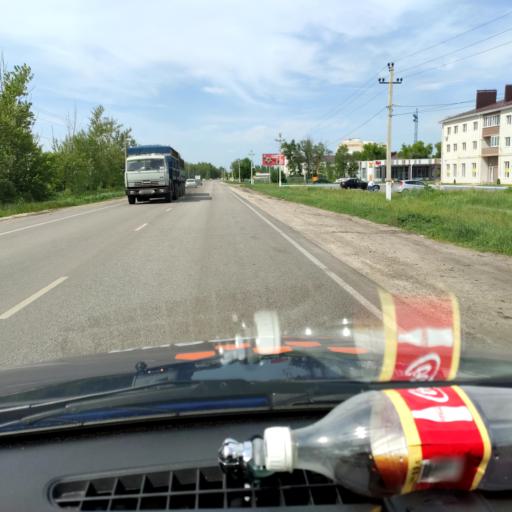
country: RU
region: Voronezj
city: Novaya Usman'
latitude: 51.6025
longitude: 39.3734
